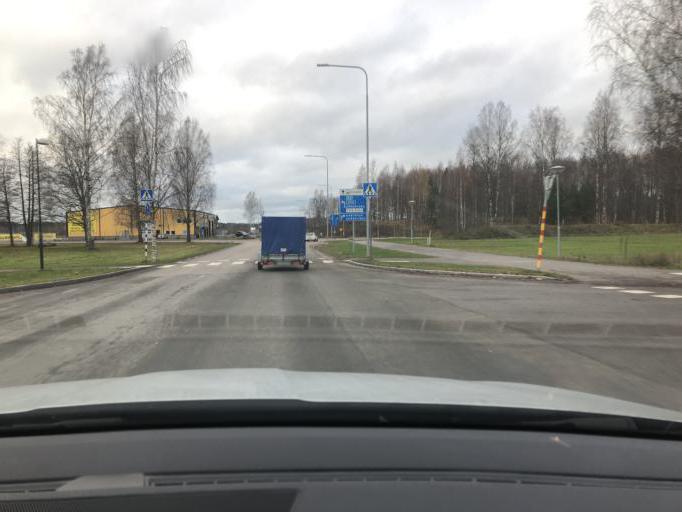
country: SE
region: Uppsala
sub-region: Tierps Kommun
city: Tierp
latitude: 60.3479
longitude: 17.4993
